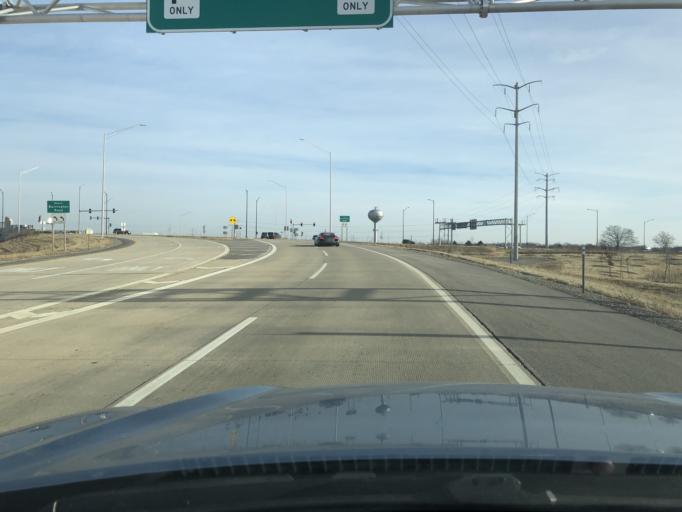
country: US
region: Illinois
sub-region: Cook County
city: South Barrington
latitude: 42.0659
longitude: -88.1470
